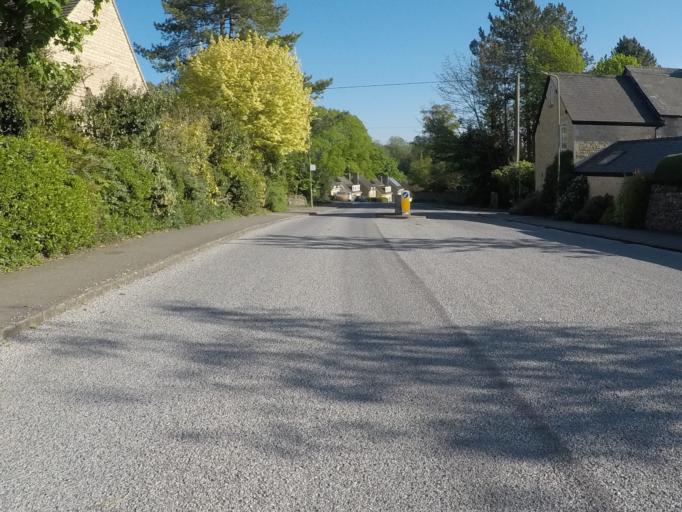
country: GB
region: England
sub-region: Oxfordshire
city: Charlbury
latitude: 51.8740
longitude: -1.4762
